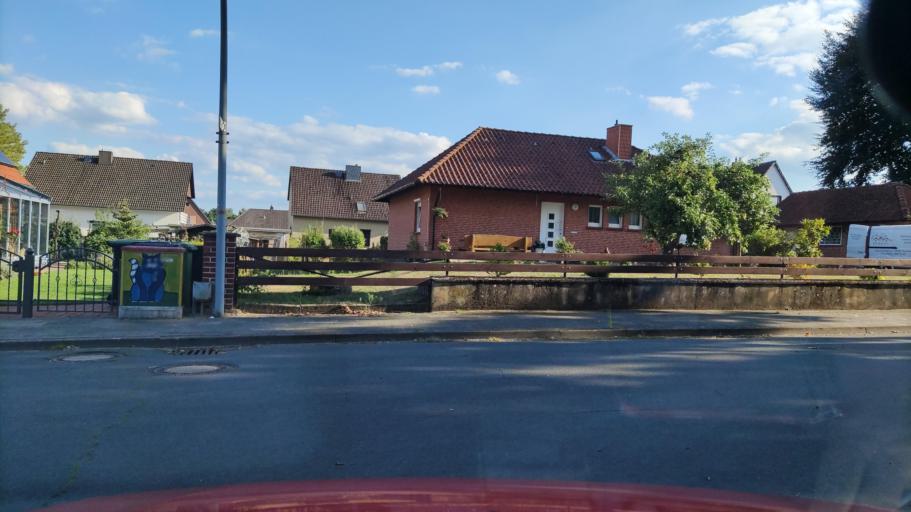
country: DE
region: Lower Saxony
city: Munster
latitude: 52.9828
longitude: 10.0933
